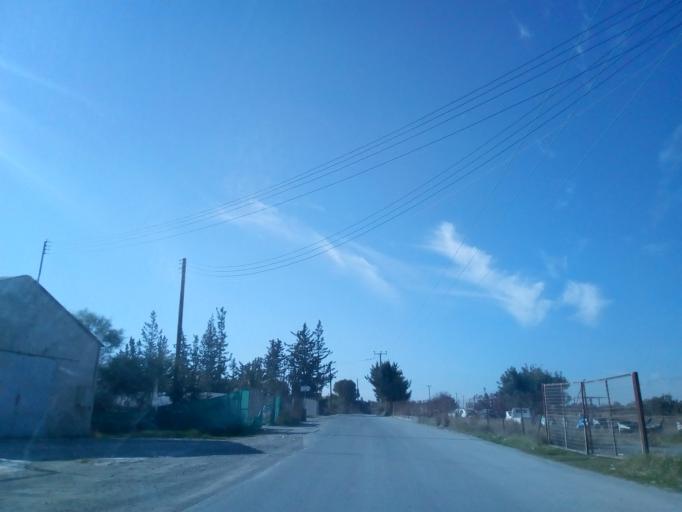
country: CY
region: Limassol
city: Ypsonas
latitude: 34.6793
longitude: 32.9806
